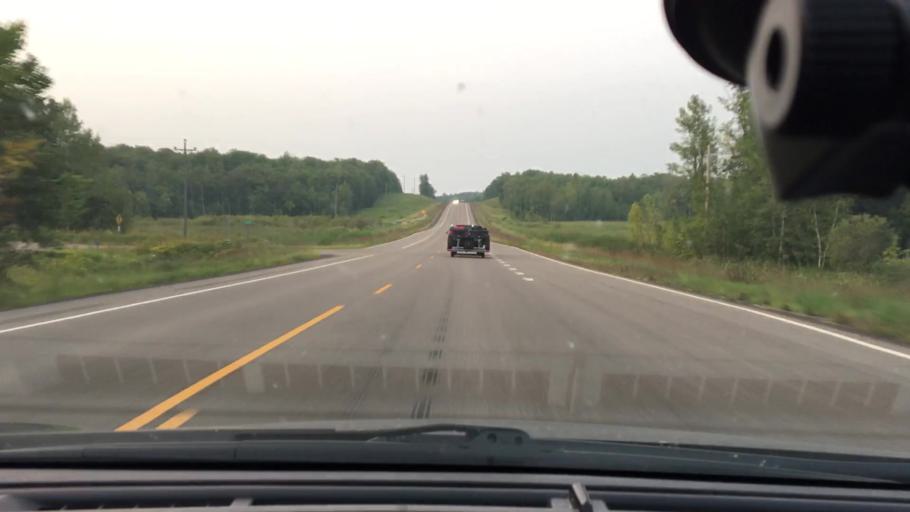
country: US
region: Minnesota
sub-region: Crow Wing County
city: Crosby
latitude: 46.6140
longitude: -93.9482
